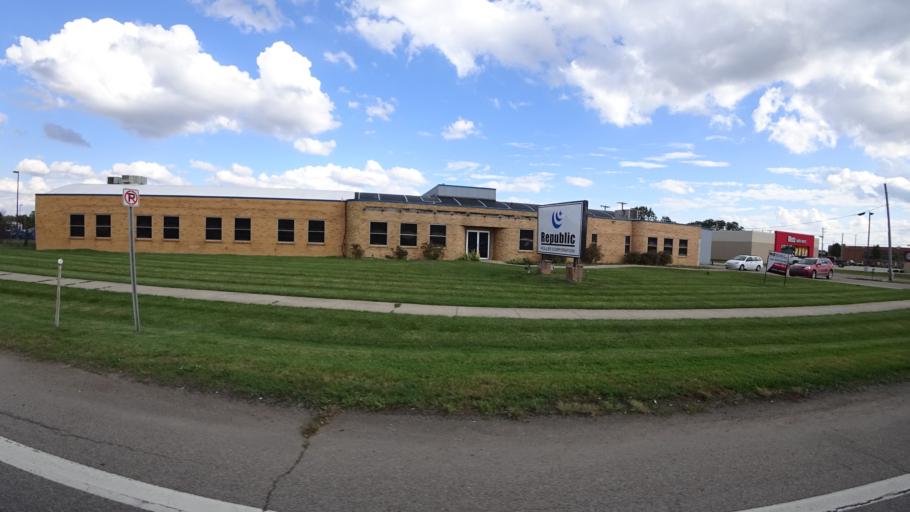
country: US
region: Michigan
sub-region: Saint Joseph County
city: Three Rivers
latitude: 41.9408
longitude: -85.6514
